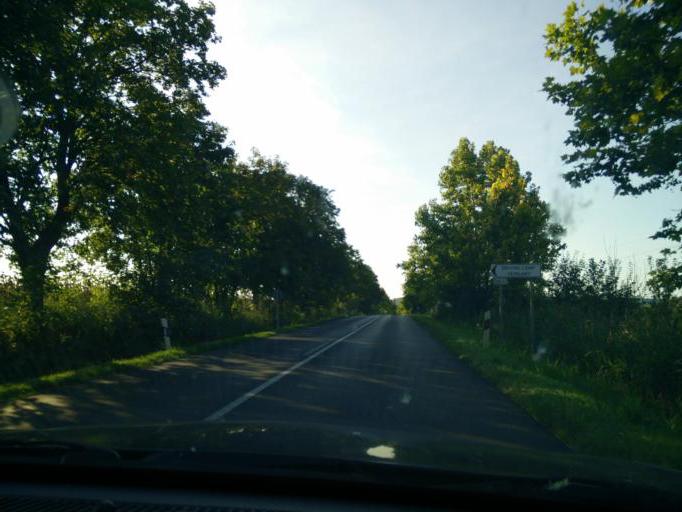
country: HU
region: Pest
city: Zsambek
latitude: 47.5208
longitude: 18.7469
